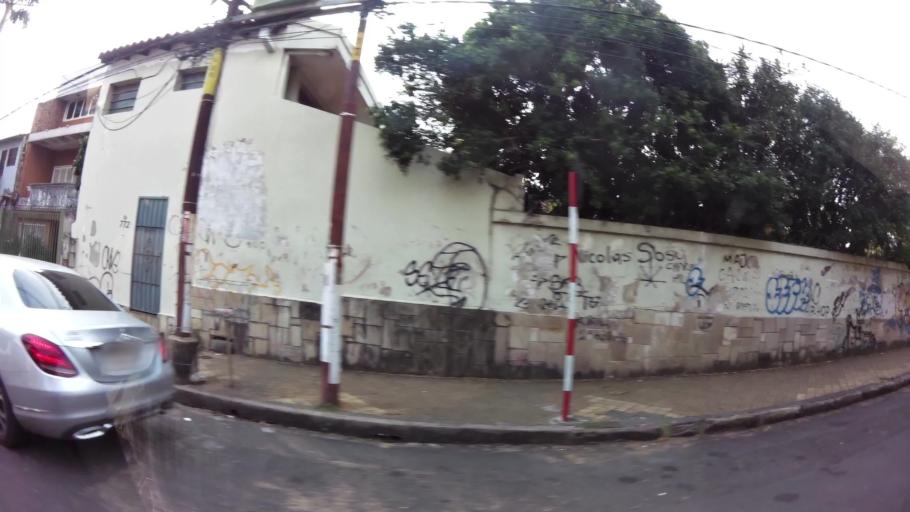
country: PY
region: Asuncion
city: Asuncion
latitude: -25.2954
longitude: -57.6195
